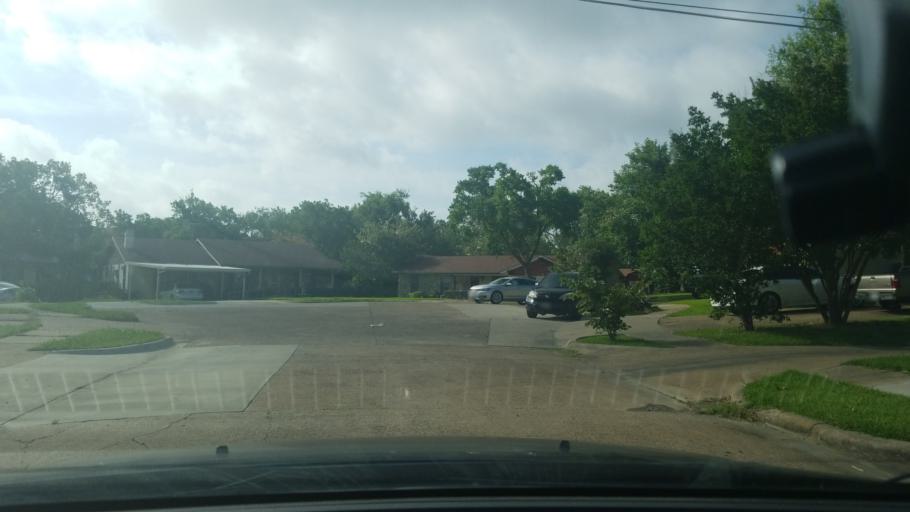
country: US
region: Texas
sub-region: Dallas County
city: Mesquite
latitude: 32.7703
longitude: -96.6379
